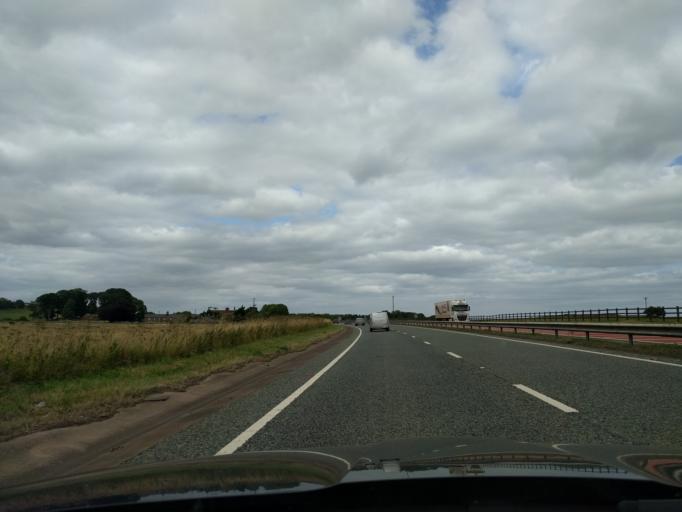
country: GB
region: England
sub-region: Northumberland
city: Ellingham
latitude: 55.4976
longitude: -1.7323
